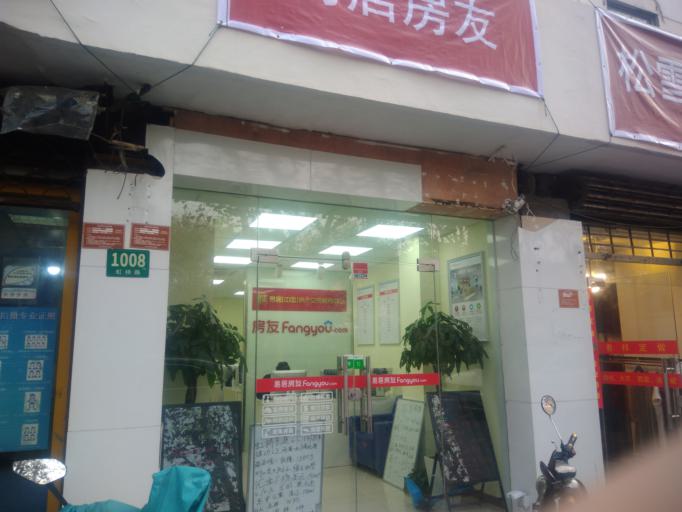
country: CN
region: Shanghai Shi
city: Changning
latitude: 31.1974
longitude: 121.4153
